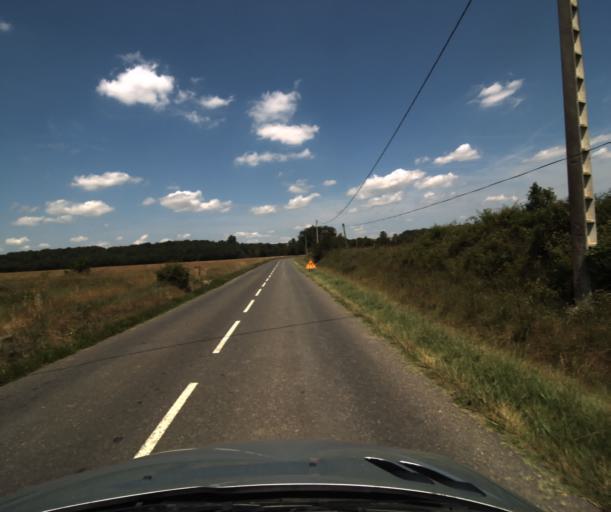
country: FR
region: Midi-Pyrenees
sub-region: Departement de la Haute-Garonne
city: Labastidette
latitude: 43.4871
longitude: 1.2136
